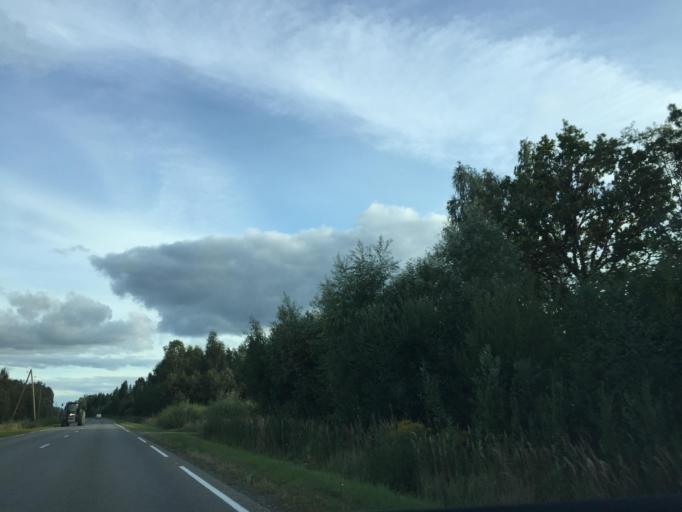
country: LV
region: Nereta
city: Nereta
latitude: 56.3105
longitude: 25.0984
